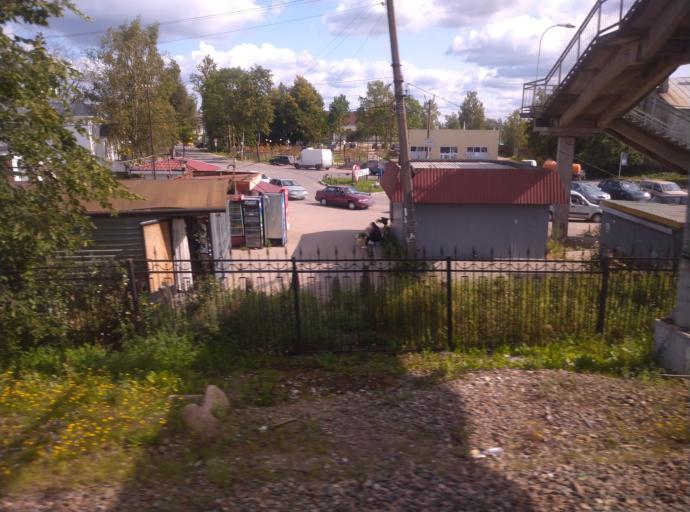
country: RU
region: Leningrad
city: Ul'yanovka
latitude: 59.6360
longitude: 30.7569
